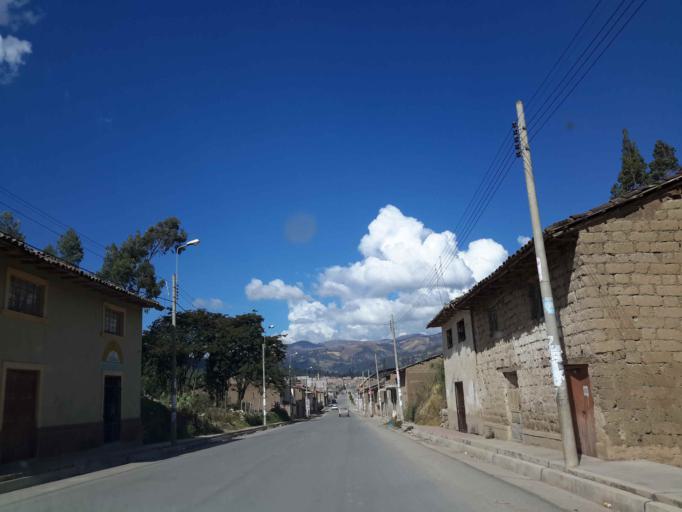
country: PE
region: Apurimac
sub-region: Provincia de Andahuaylas
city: Talavera
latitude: -13.6509
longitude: -73.4393
